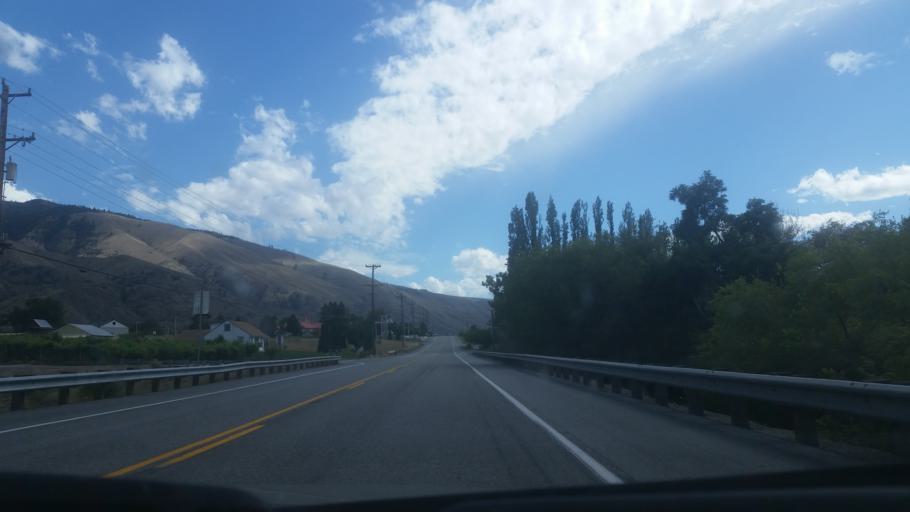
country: US
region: Washington
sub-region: Chelan County
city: Entiat
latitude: 47.6286
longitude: -120.2281
